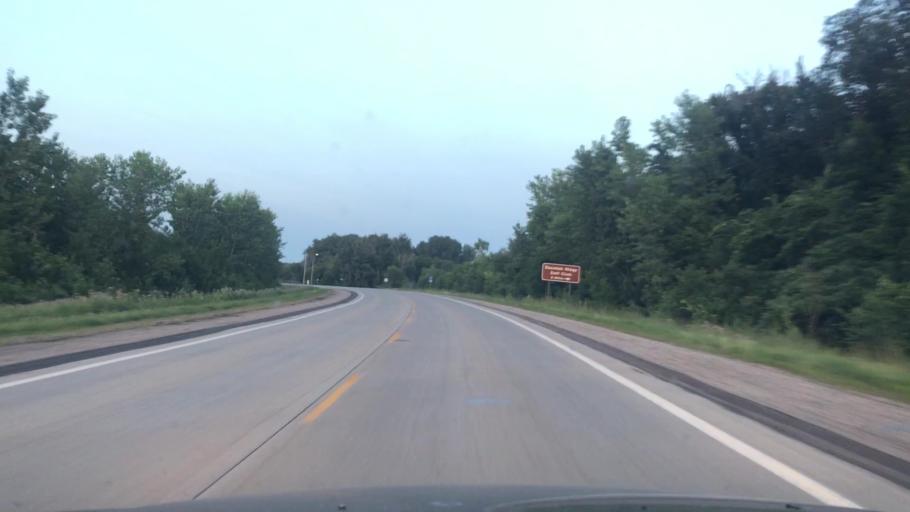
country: US
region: Minnesota
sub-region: Redwood County
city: Redwood Falls
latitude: 44.5402
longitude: -95.0101
